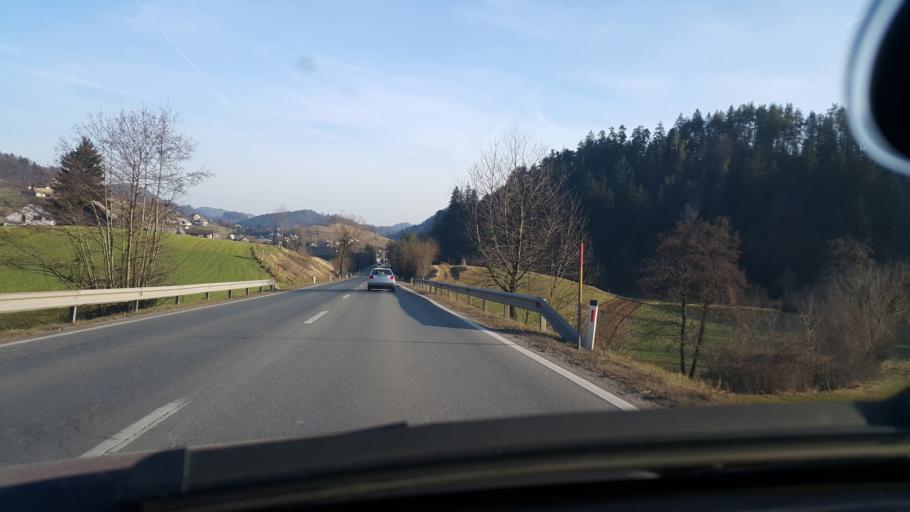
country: SI
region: Velenje
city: Velenje
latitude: 46.3437
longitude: 15.1660
